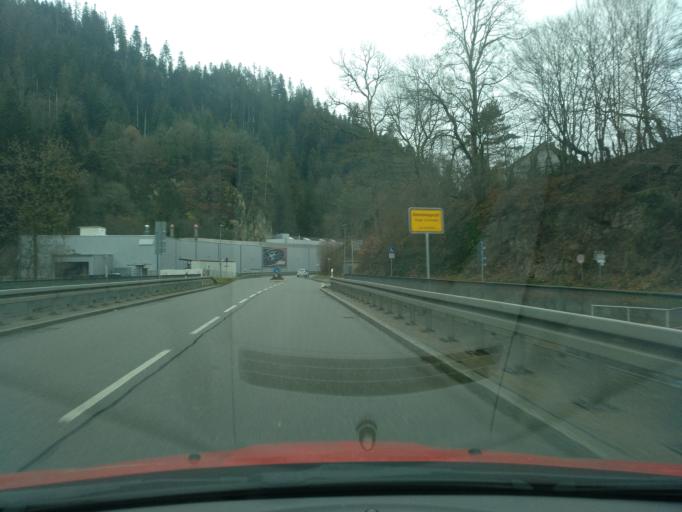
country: DE
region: Baden-Wuerttemberg
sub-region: Freiburg Region
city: Schenkenzell
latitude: 48.2633
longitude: 8.3689
